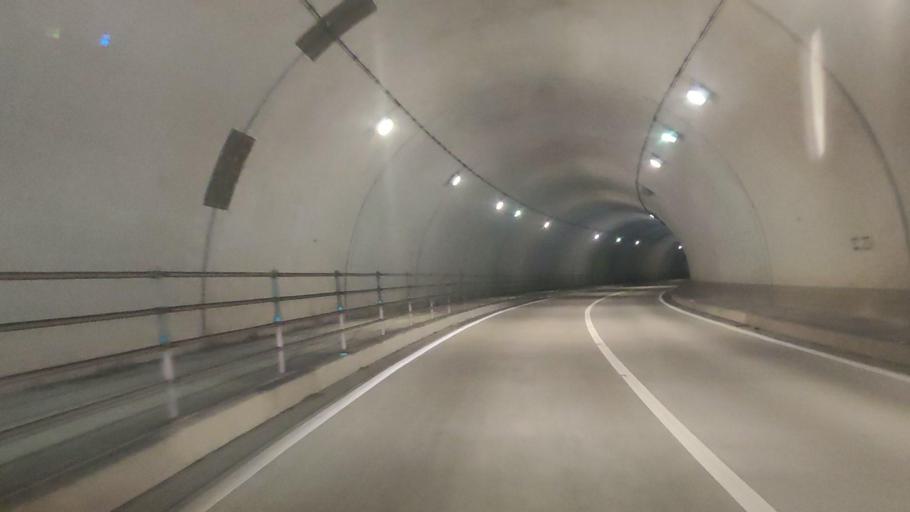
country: JP
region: Oita
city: Saiki
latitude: 32.8058
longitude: 131.8963
